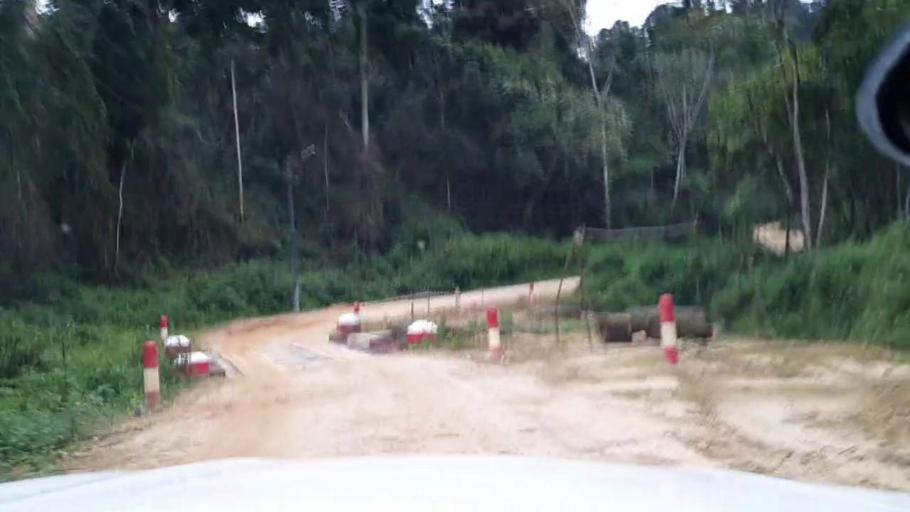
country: RW
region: Western Province
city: Cyangugu
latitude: -2.5695
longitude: 29.2253
